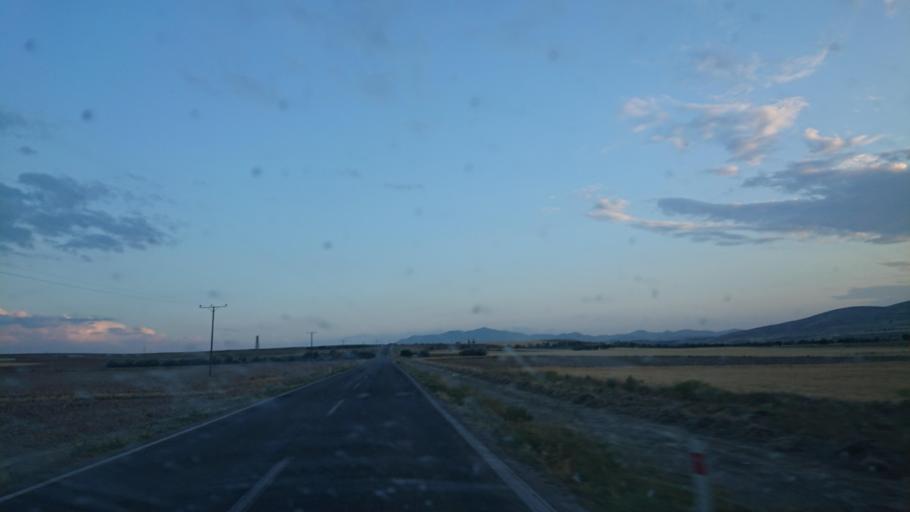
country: TR
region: Aksaray
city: Balci
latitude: 38.8084
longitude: 34.1318
